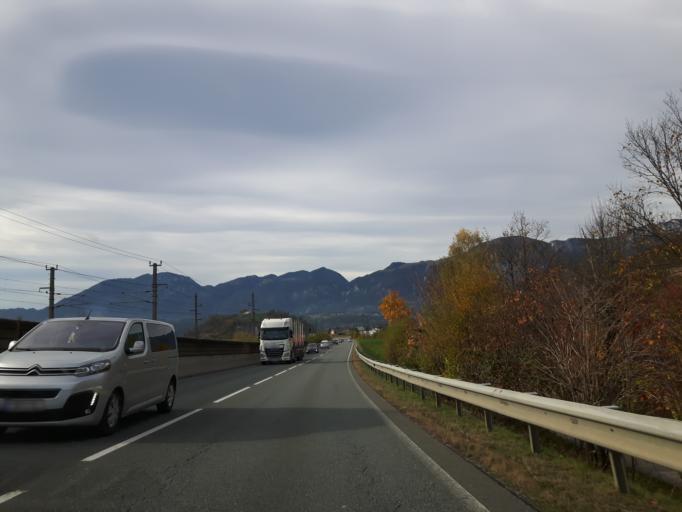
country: AT
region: Tyrol
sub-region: Politischer Bezirk Kufstein
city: Bad Haering
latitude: 47.4909
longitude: 12.1011
